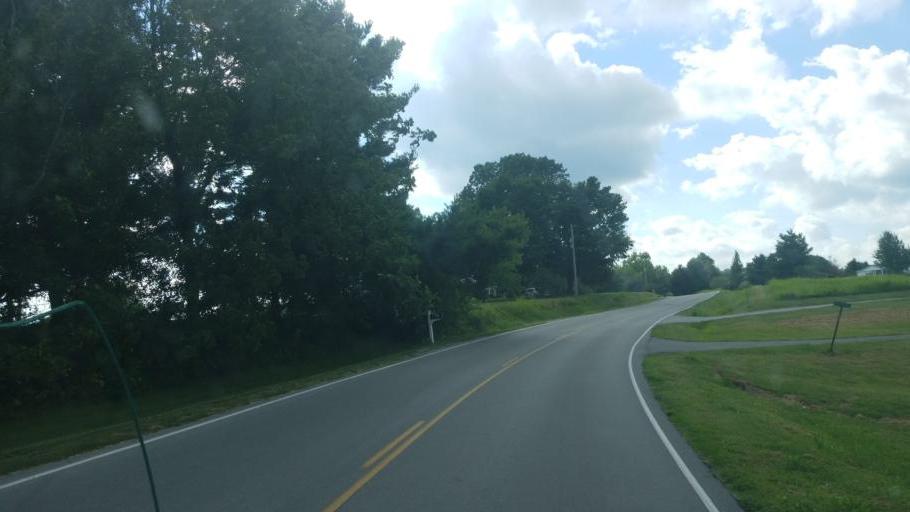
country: US
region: Illinois
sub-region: Union County
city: Cobden
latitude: 37.5464
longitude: -89.2836
